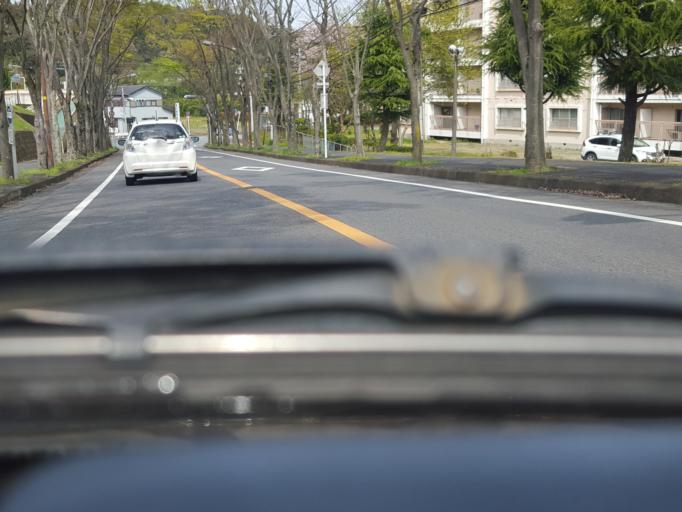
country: JP
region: Chiba
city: Ichihara
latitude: 35.4554
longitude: 140.0511
